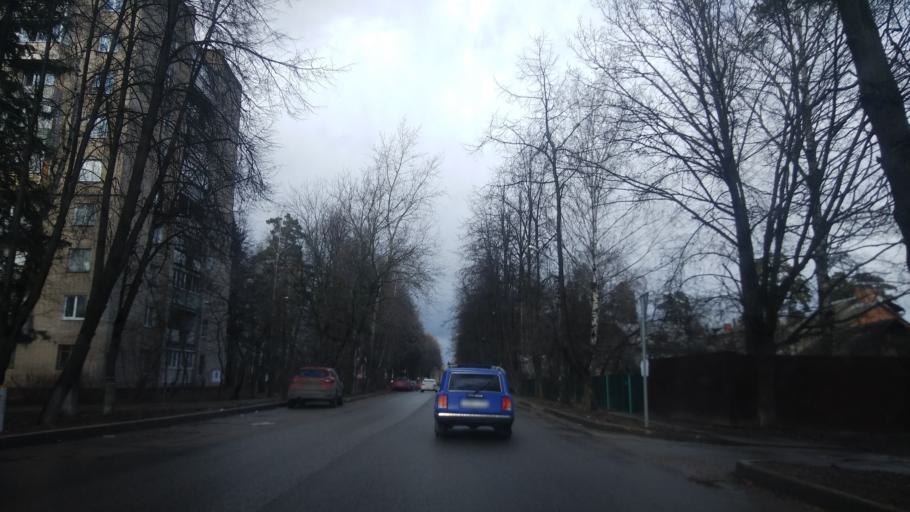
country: RU
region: Moskovskaya
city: Mamontovka
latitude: 56.0066
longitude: 37.8298
